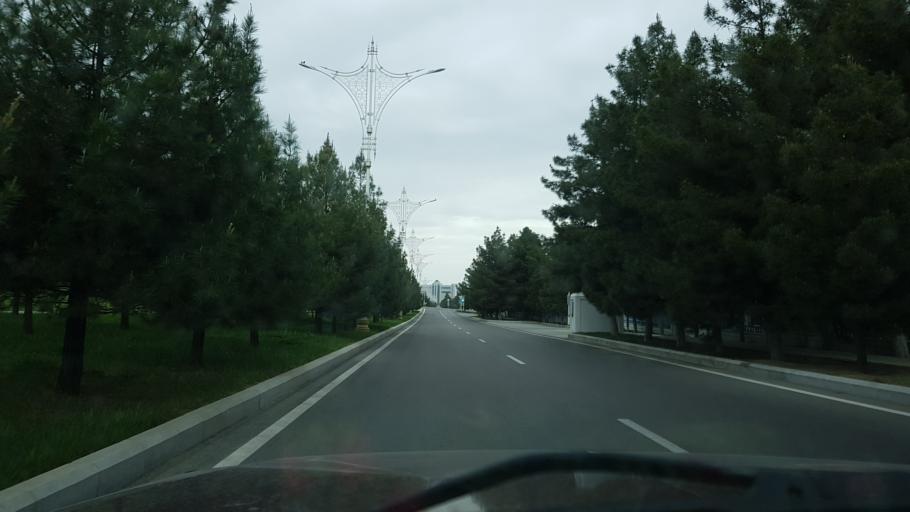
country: TM
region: Ahal
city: Ashgabat
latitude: 37.8871
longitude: 58.3546
